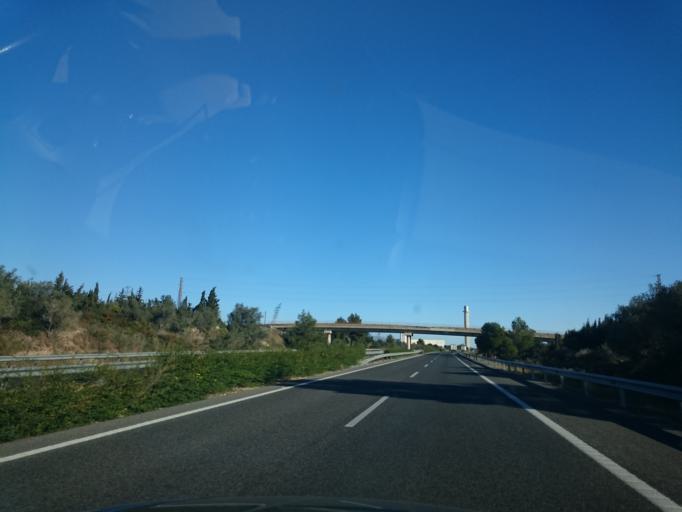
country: ES
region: Catalonia
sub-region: Provincia de Tarragona
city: Camarles
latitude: 40.7954
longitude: 0.6673
